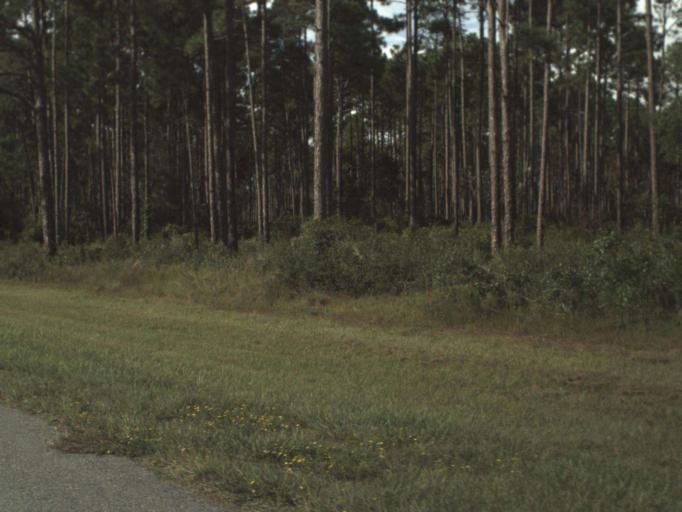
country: US
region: Florida
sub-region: Bay County
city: Mexico Beach
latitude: 30.0060
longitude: -85.5073
